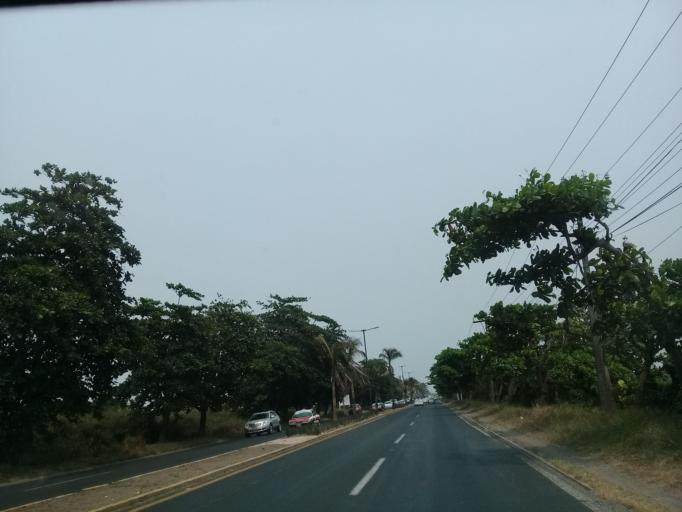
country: MX
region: Veracruz
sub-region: Veracruz
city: Hacienda Sotavento
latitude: 19.1460
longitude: -96.1649
